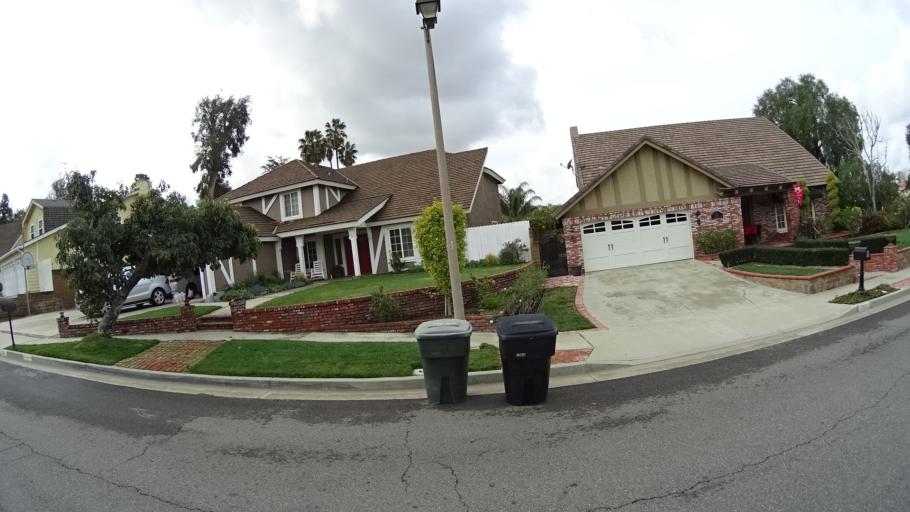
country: US
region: California
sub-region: Orange County
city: Yorba Linda
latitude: 33.8526
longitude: -117.7735
